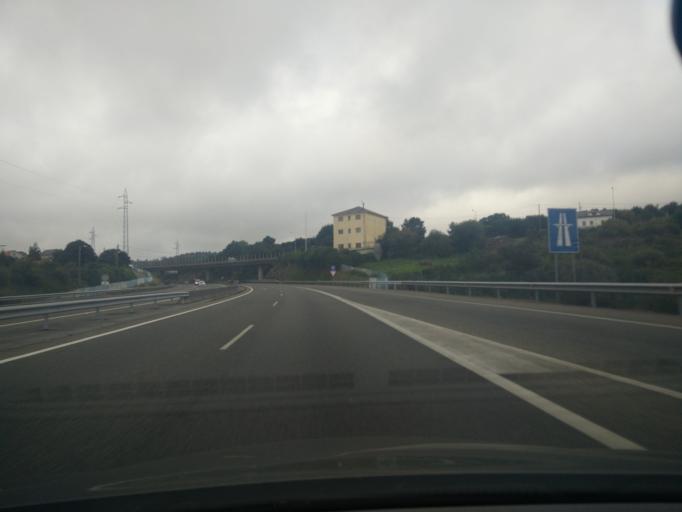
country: ES
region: Galicia
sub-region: Provincia da Coruna
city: Laracha
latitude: 43.2667
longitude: -8.5407
